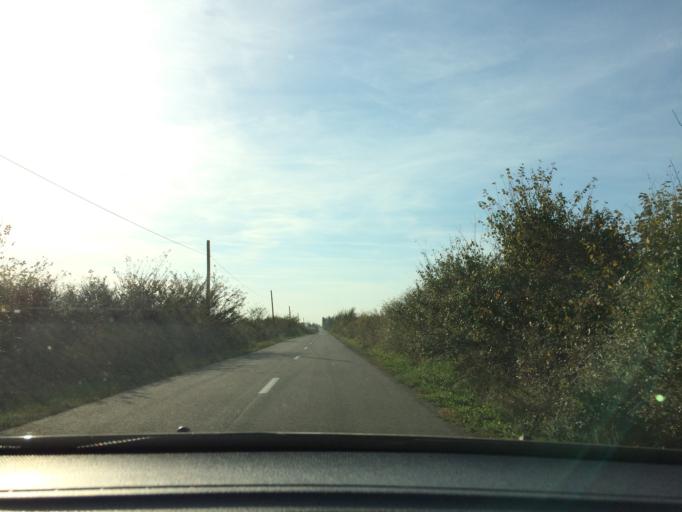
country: RO
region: Timis
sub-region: Oras Recas
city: Recas
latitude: 45.8092
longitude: 21.5422
